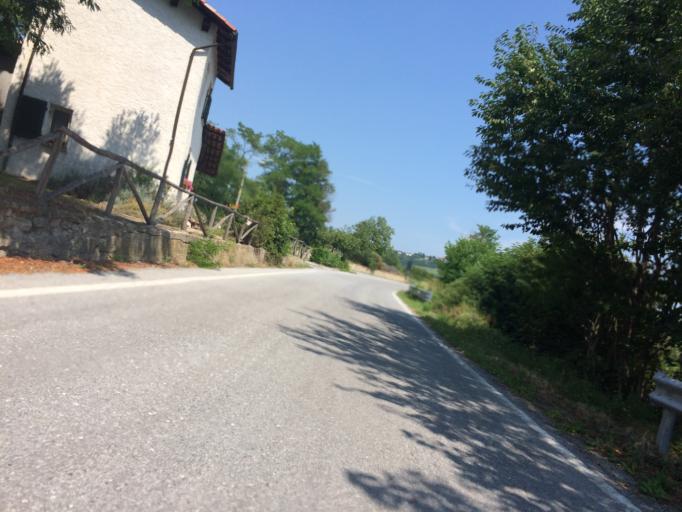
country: IT
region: Piedmont
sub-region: Provincia di Cuneo
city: Cissone
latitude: 44.5616
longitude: 8.0345
